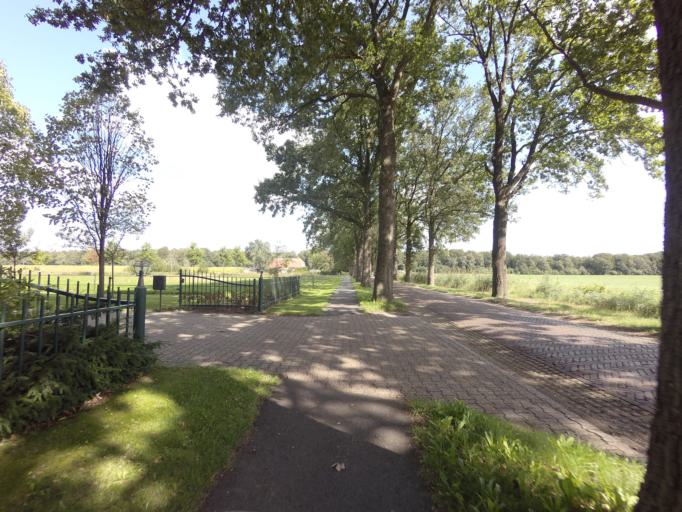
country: NL
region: Overijssel
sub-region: Gemeente Staphorst
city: Staphorst
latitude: 52.6147
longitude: 6.2649
